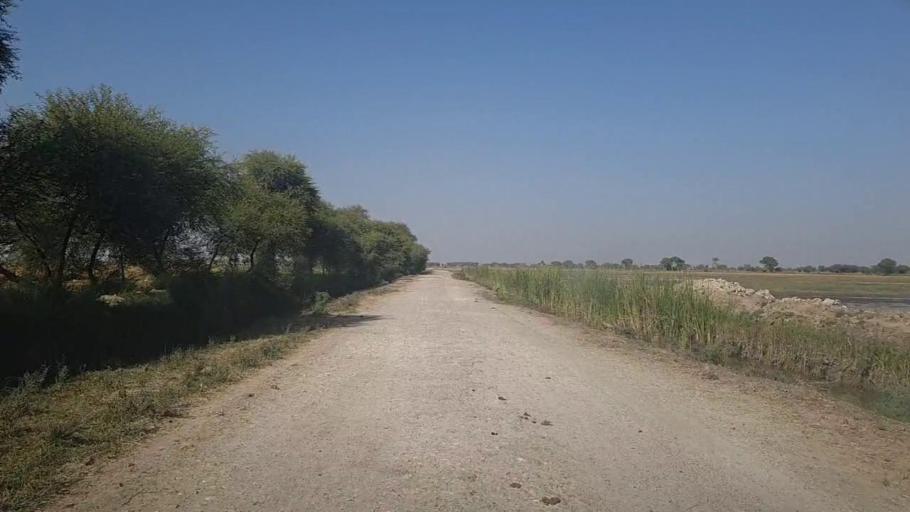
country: PK
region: Sindh
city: Thul
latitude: 28.3043
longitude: 68.7709
